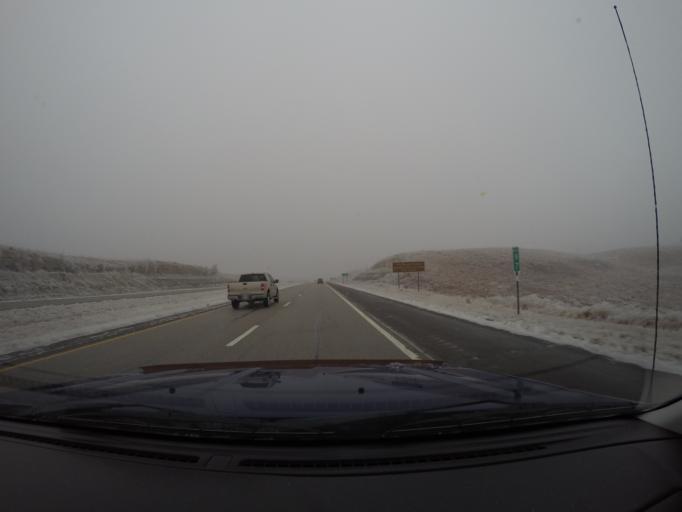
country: US
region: Kansas
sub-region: Riley County
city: Manhattan
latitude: 39.0720
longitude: -96.5382
